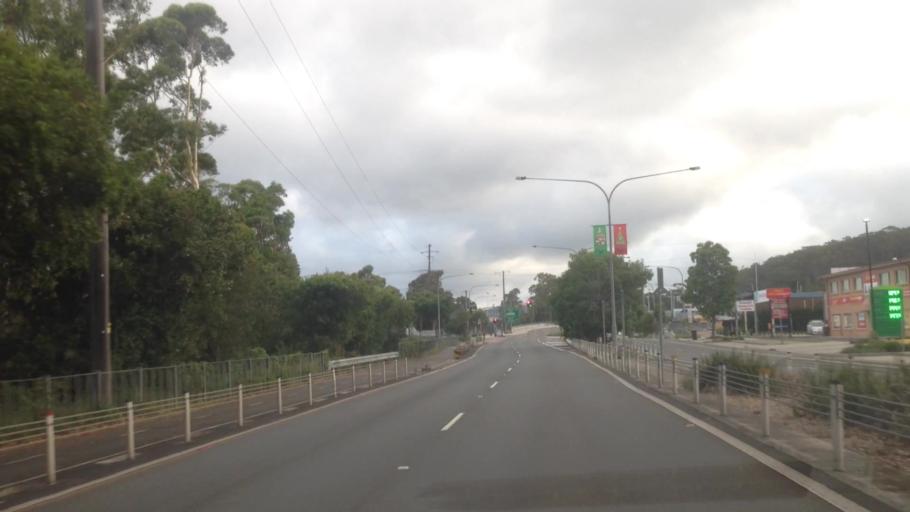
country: AU
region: New South Wales
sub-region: Wyong Shire
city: Chittaway Bay
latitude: -33.3055
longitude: 151.4203
